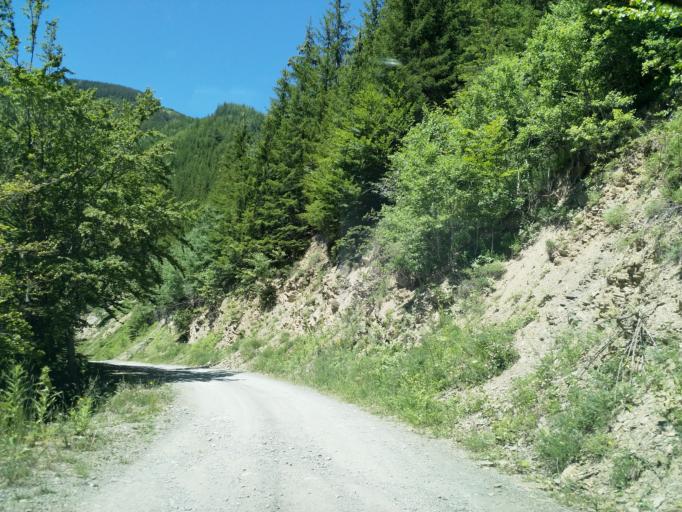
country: XK
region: Mitrovica
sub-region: Komuna e Leposaviqit
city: Leposaviq
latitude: 43.2776
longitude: 20.8714
